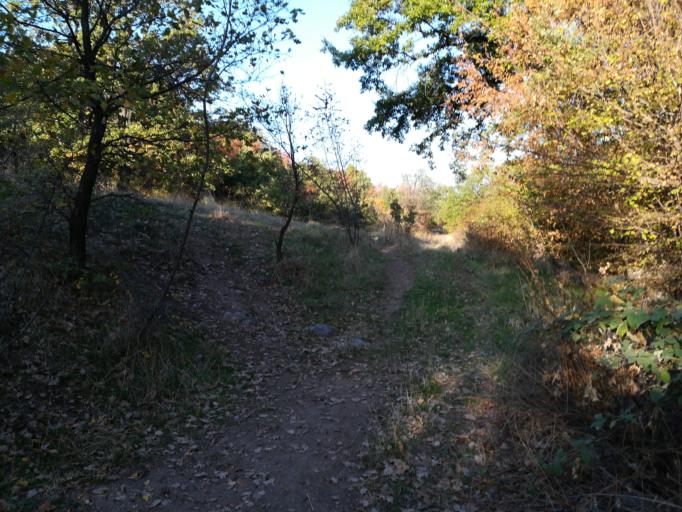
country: BG
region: Khaskovo
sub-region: Obshtina Mineralni Bani
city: Mineralni Bani
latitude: 41.9826
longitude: 25.2358
